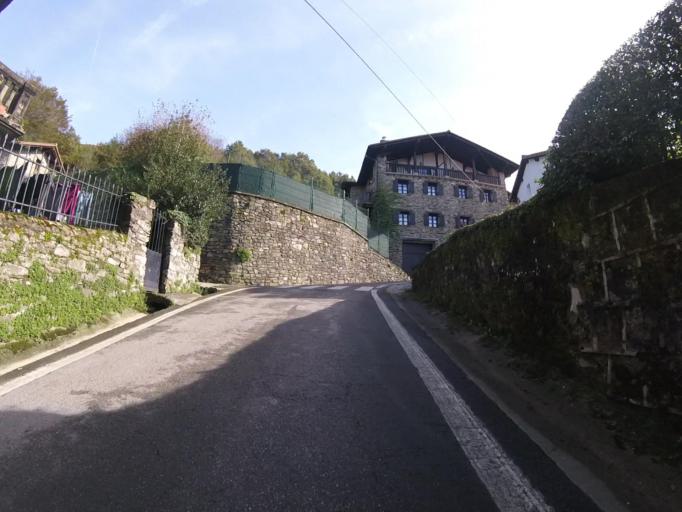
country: ES
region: Navarre
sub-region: Provincia de Navarra
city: Arano
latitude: 43.2001
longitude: -1.8954
